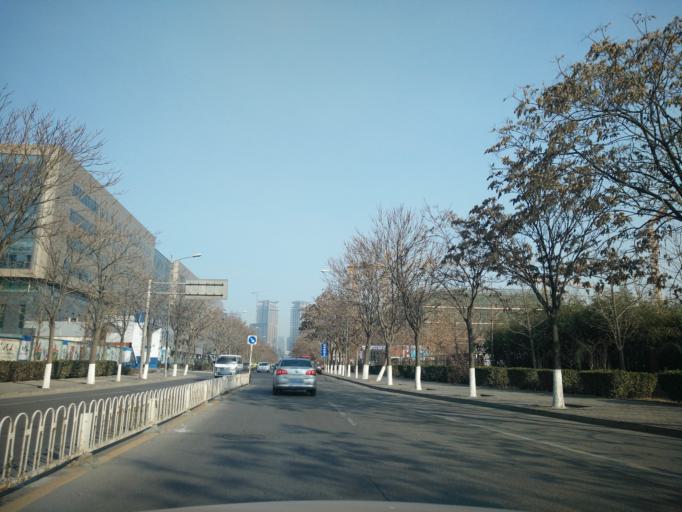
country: CN
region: Beijing
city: Jiugong
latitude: 39.7771
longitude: 116.4990
